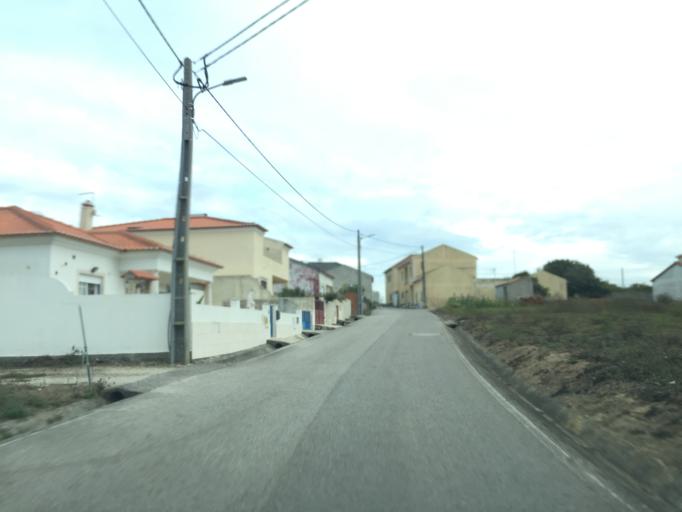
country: PT
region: Leiria
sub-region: Peniche
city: Atouguia da Baleia
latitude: 39.3425
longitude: -9.2949
